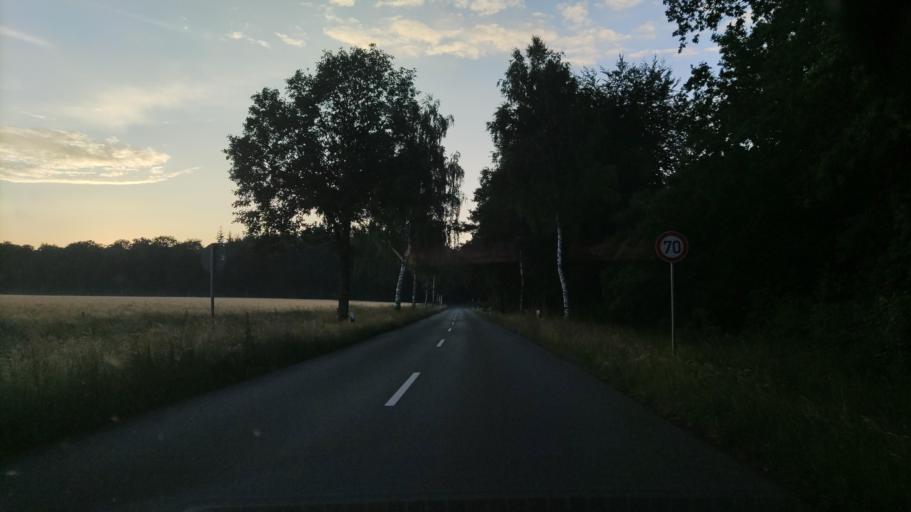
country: DE
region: Lower Saxony
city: Bispingen
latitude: 53.1205
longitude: 10.0549
